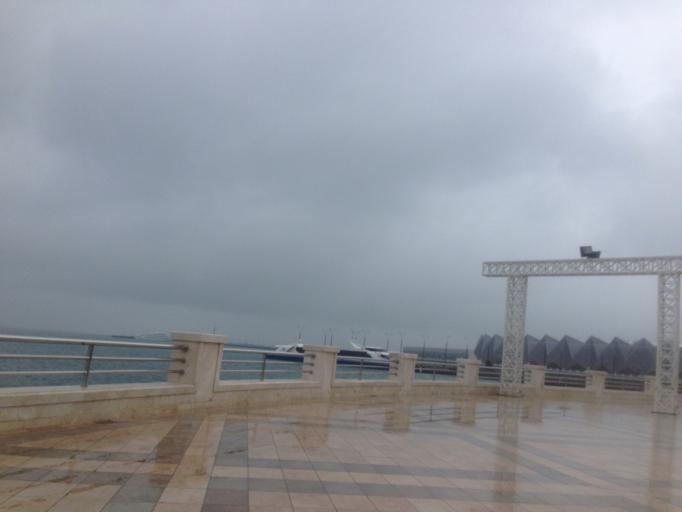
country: AZ
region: Baki
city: Badamdar
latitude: 40.3479
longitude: 49.8463
